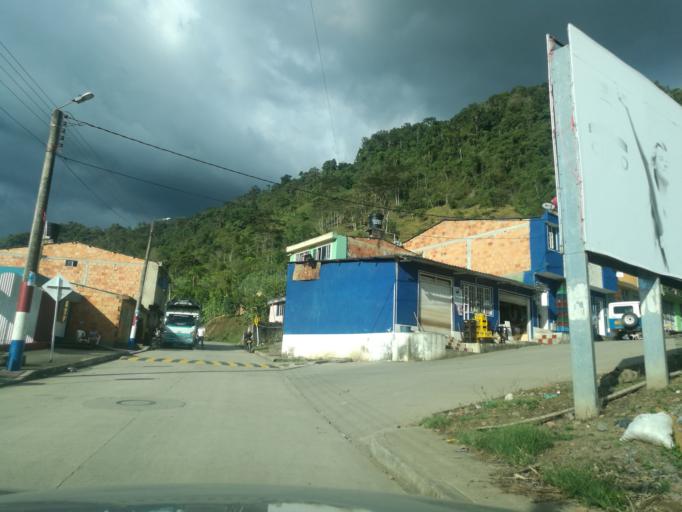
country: CO
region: Boyaca
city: Maripi
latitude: 5.5506
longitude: -74.0025
